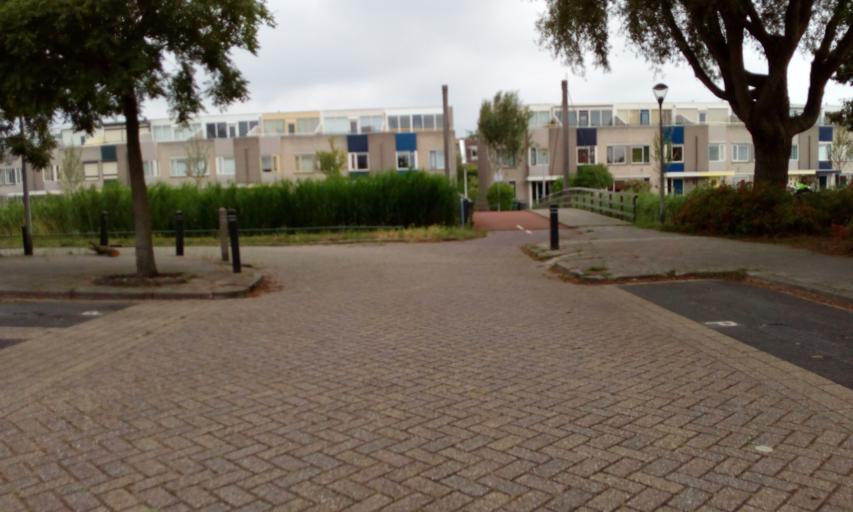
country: NL
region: South Holland
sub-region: Gemeente Pijnacker-Nootdorp
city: Pijnacker
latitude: 52.0131
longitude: 4.4504
